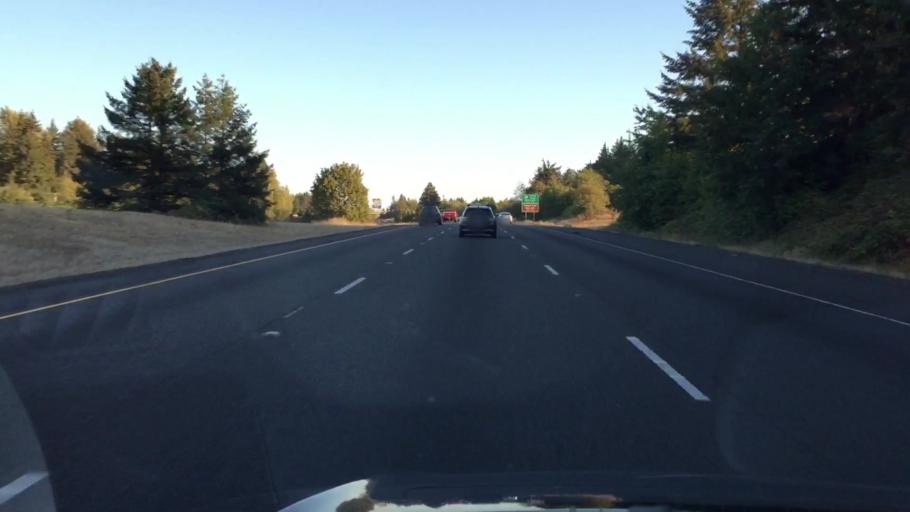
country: US
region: Washington
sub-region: Clark County
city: La Center
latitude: 45.8608
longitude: -122.7061
